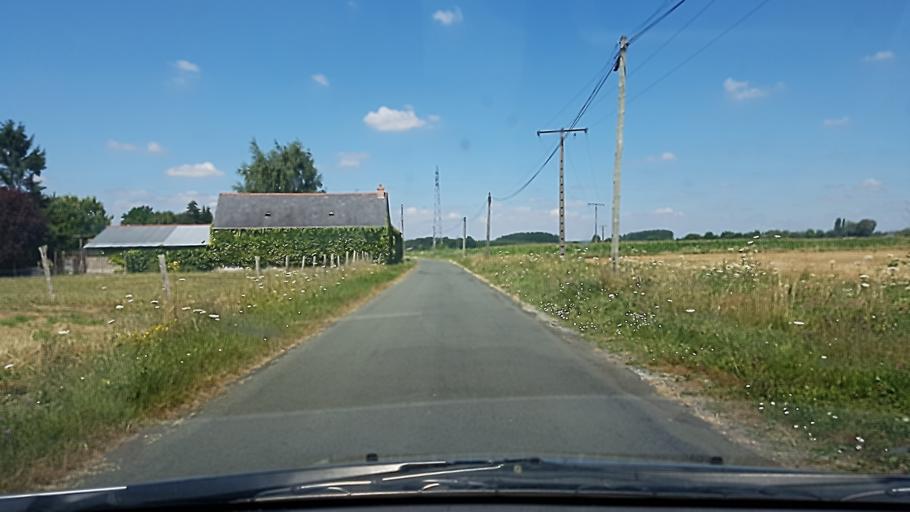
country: FR
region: Pays de la Loire
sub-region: Departement de Maine-et-Loire
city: Corze
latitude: 47.5426
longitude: -0.3859
